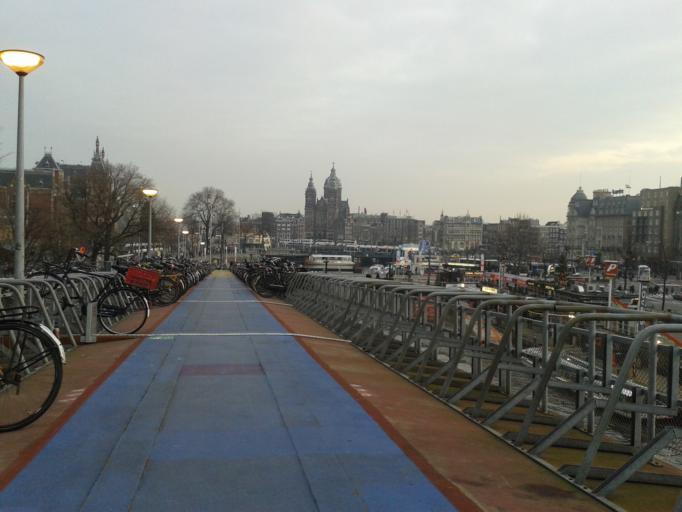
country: NL
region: North Holland
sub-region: Gemeente Amsterdam
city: Amsterdam
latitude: 52.3796
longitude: 4.8964
